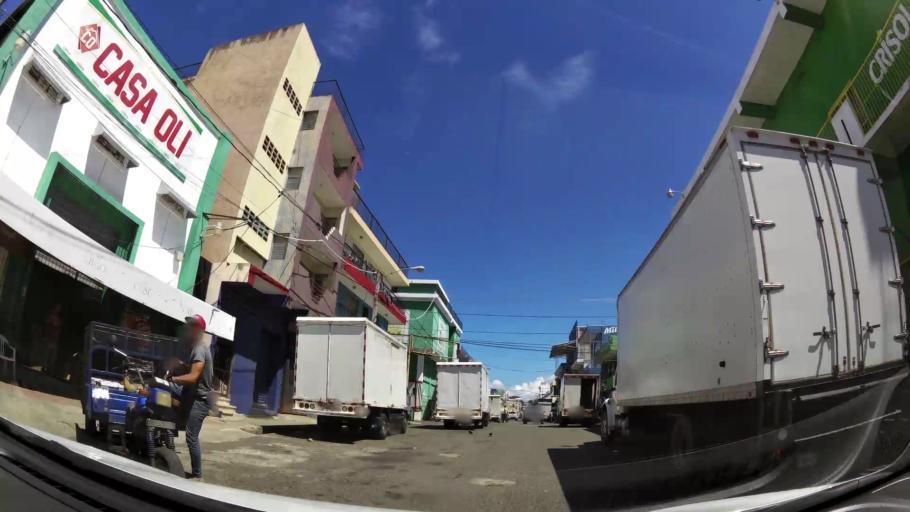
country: DO
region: Santiago
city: Santiago de los Caballeros
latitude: 19.4531
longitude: -70.7119
